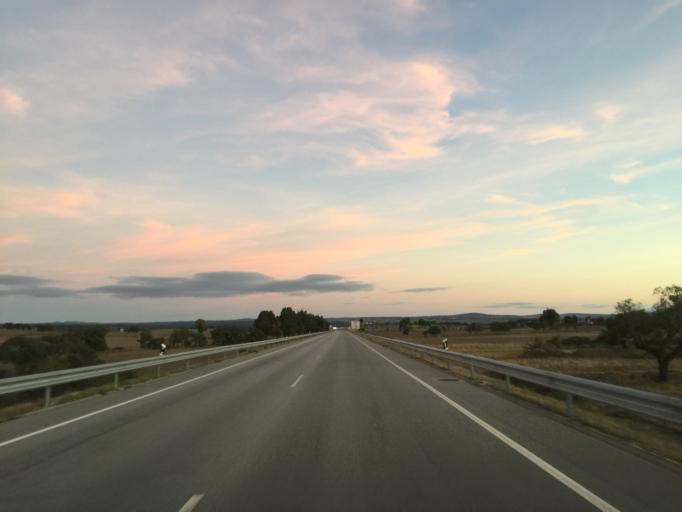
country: PT
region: Portalegre
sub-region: Alter do Chao
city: Alter do Chao
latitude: 39.3011
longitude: -7.6350
